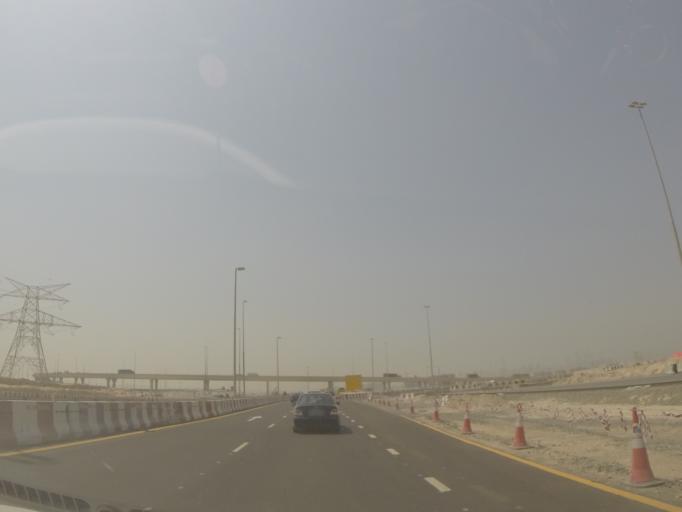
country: AE
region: Dubai
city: Dubai
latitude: 25.0143
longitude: 55.1633
